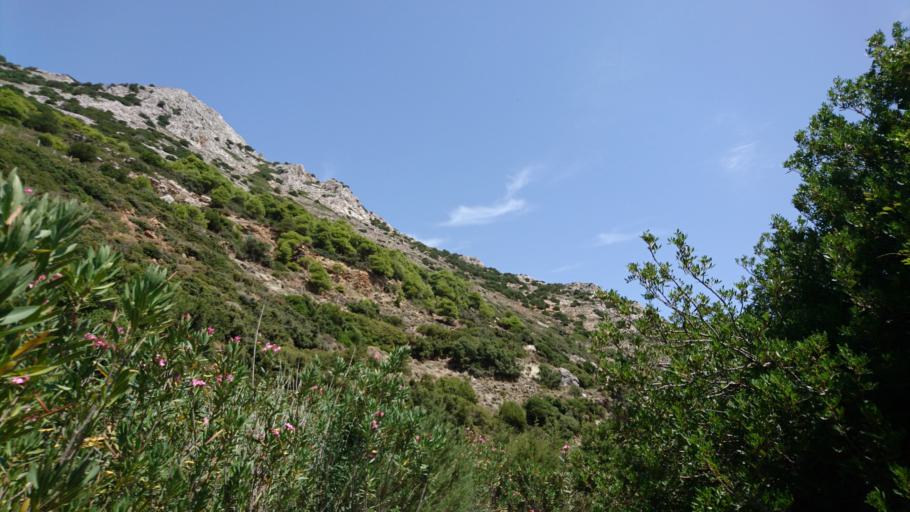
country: GR
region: Central Greece
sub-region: Nomos Evvoias
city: Skyros
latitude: 38.9041
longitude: 24.5501
